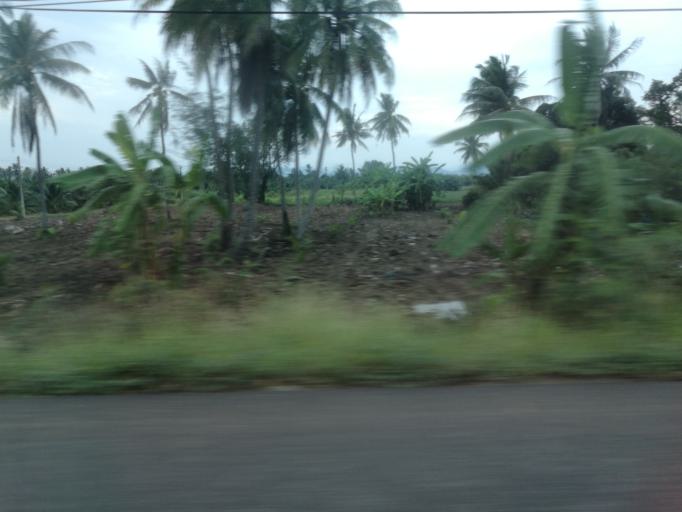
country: TH
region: Prachuap Khiri Khan
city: Prachuap Khiri Khan
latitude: 11.8853
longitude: 99.7889
